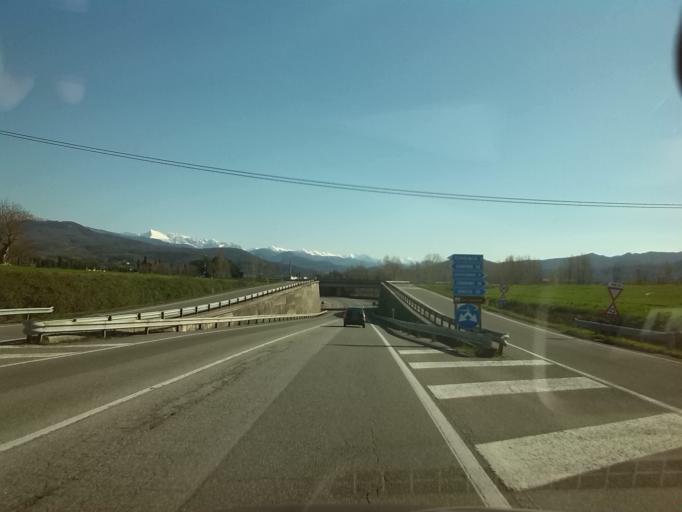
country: IT
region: Friuli Venezia Giulia
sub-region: Provincia di Udine
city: Premariacco
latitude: 46.0851
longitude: 13.4015
